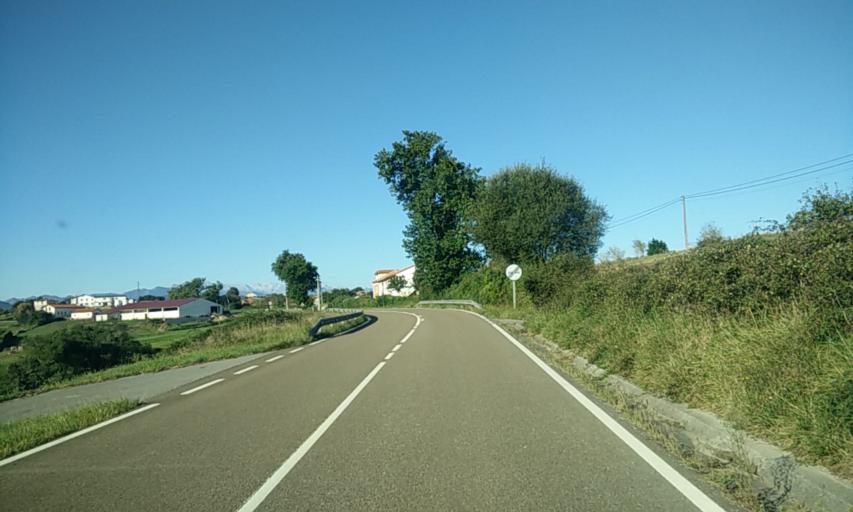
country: ES
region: Cantabria
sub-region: Provincia de Cantabria
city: San Vicente de la Barquera
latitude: 43.3814
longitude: -4.3566
